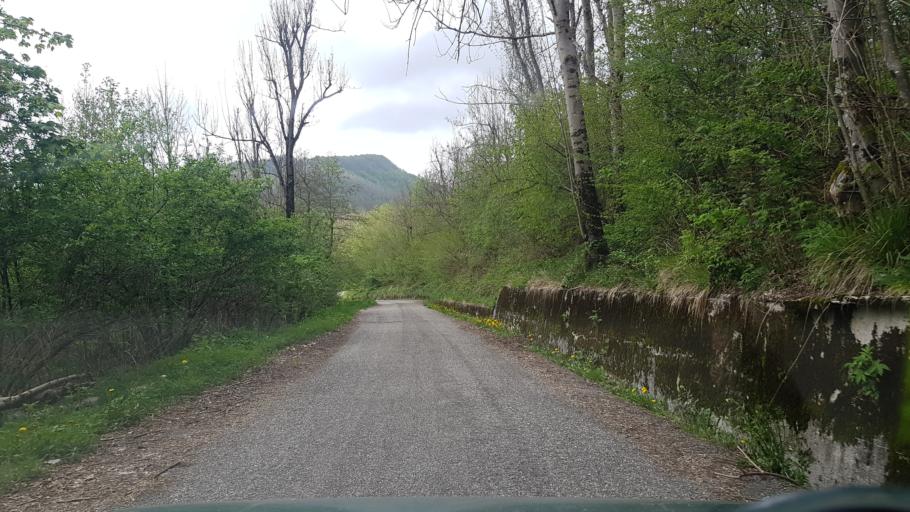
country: IT
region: Friuli Venezia Giulia
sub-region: Provincia di Udine
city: Attimis
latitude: 46.2019
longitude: 13.3604
